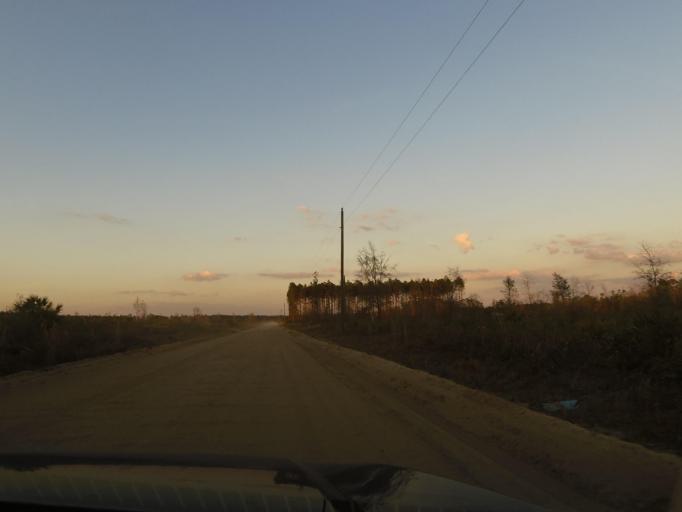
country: US
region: Florida
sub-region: Clay County
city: Green Cove Springs
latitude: 29.8983
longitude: -81.7830
